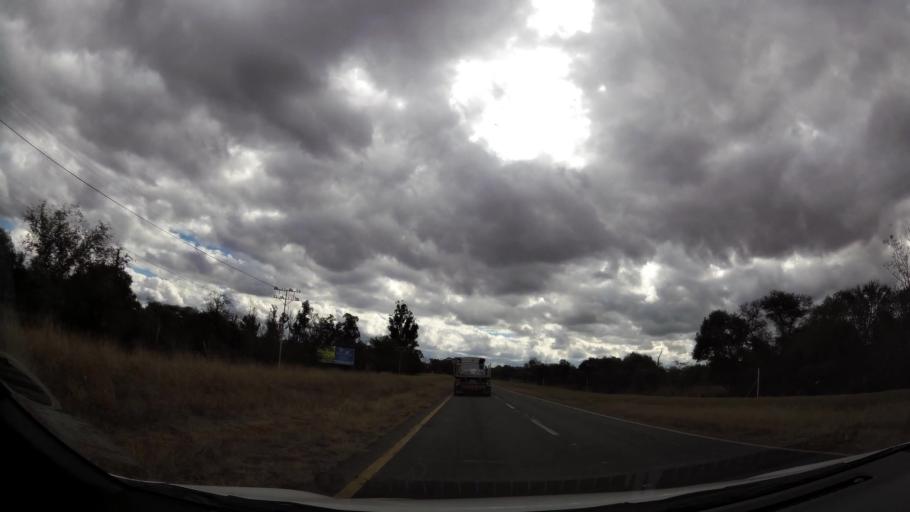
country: ZA
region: Limpopo
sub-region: Waterberg District Municipality
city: Modimolle
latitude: -24.7363
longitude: 28.4347
